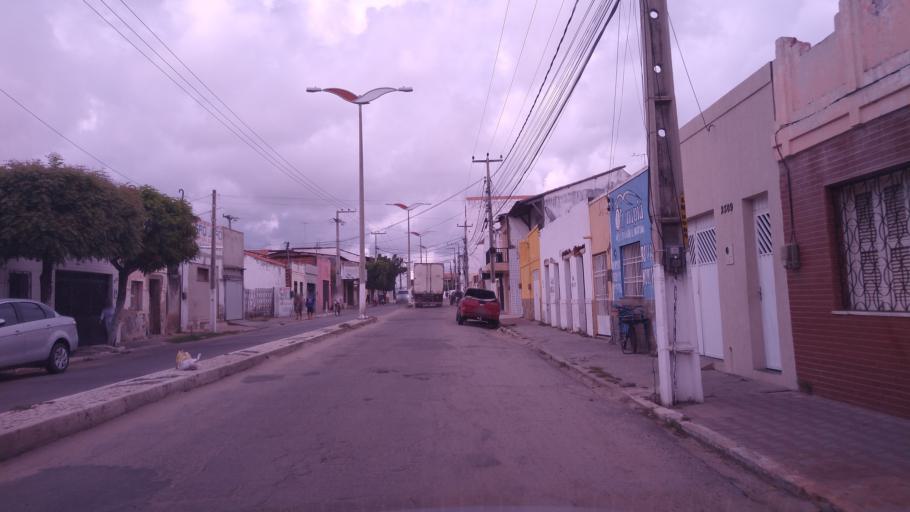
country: BR
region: Ceara
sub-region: Quixada
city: Quixada
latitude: -4.9655
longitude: -39.0159
